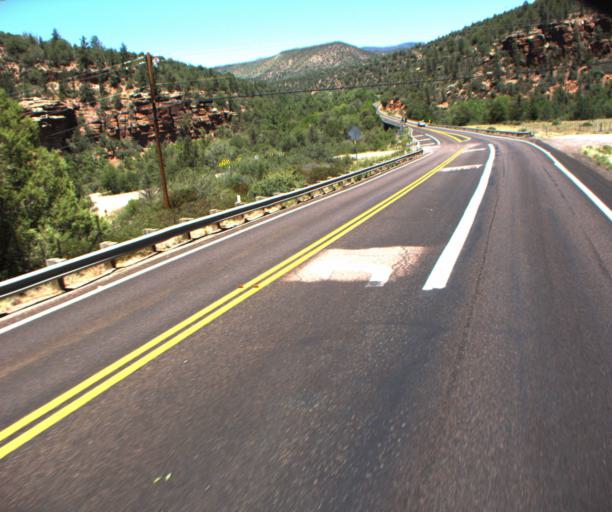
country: US
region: Arizona
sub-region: Gila County
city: Payson
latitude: 34.2990
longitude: -111.3572
